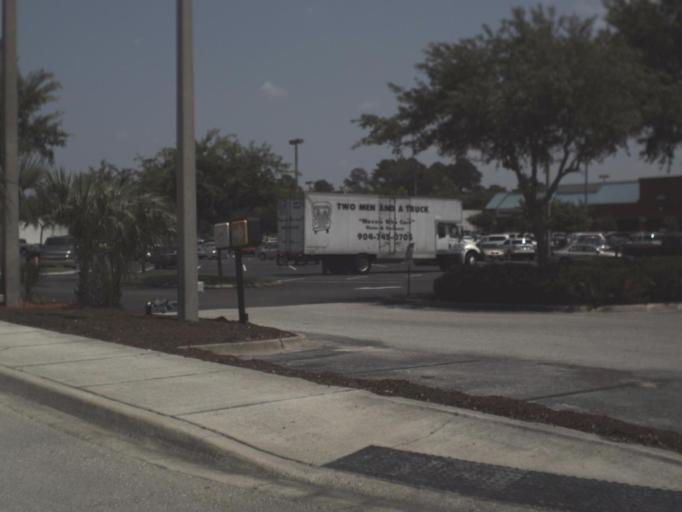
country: US
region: Florida
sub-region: Duval County
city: Jacksonville
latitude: 30.3524
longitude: -81.5496
